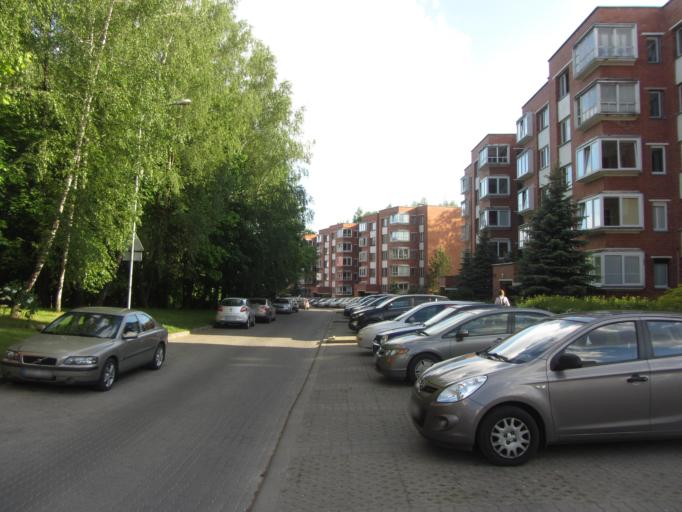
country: LT
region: Vilnius County
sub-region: Vilnius
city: Fabijoniskes
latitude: 54.7416
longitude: 25.2658
